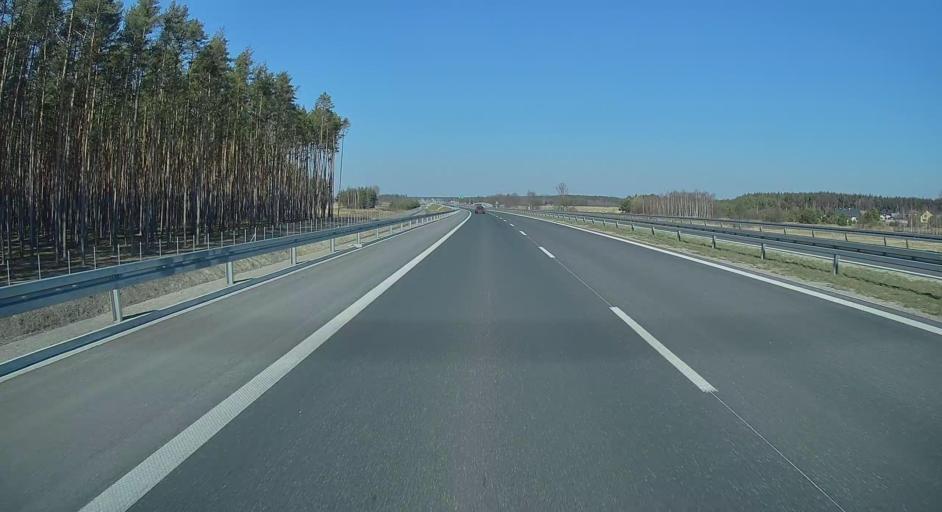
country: PL
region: Subcarpathian Voivodeship
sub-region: Powiat lezajski
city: Letownia
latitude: 50.3580
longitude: 22.1959
